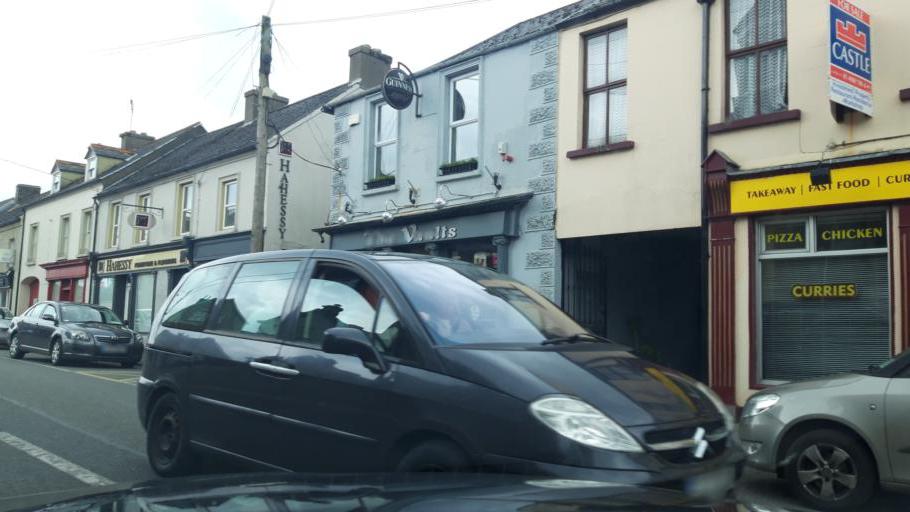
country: IE
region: Leinster
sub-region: Kilkenny
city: Castlecomer
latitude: 52.8046
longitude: -7.2103
